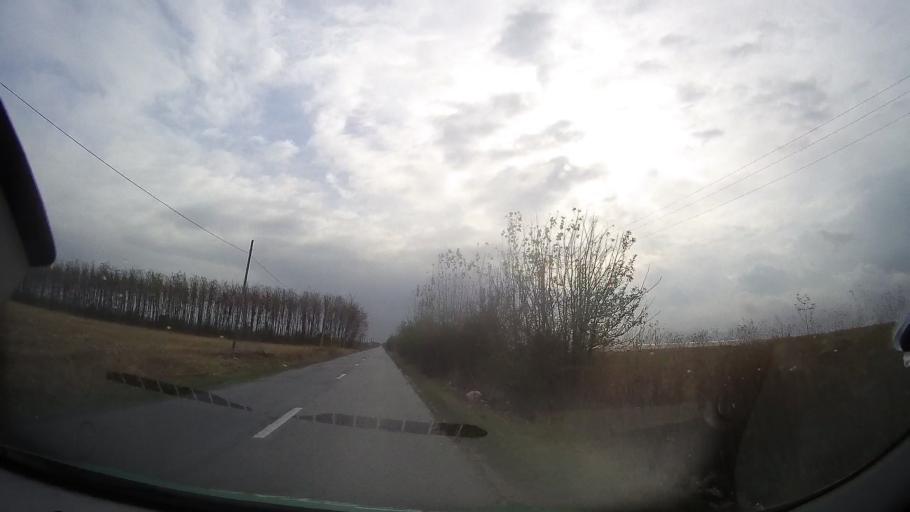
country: RO
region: Ialomita
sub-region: Comuna Fierbinti-Targ
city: Fierbintii de Jos
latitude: 44.7149
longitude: 26.3902
